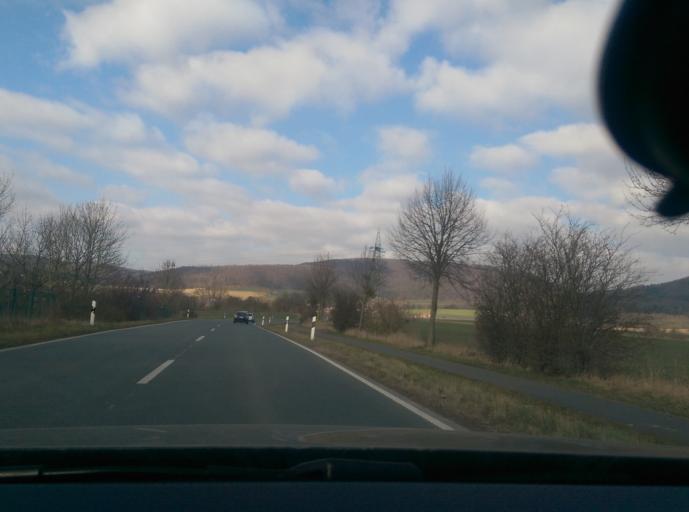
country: DE
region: Lower Saxony
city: Hessisch Oldendorf
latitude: 52.1786
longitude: 9.2536
